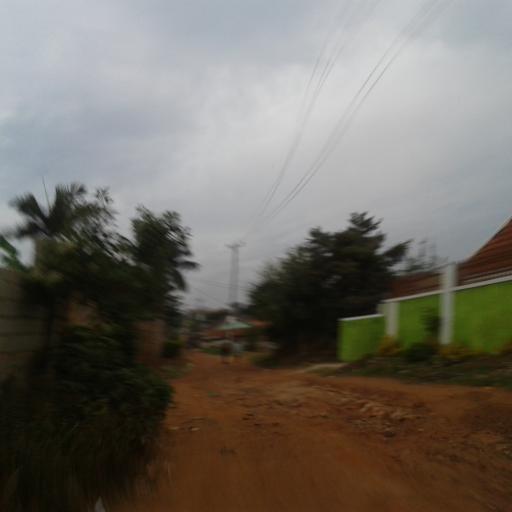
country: UG
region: Central Region
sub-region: Kampala District
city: Kampala
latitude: 0.2472
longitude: 32.6221
